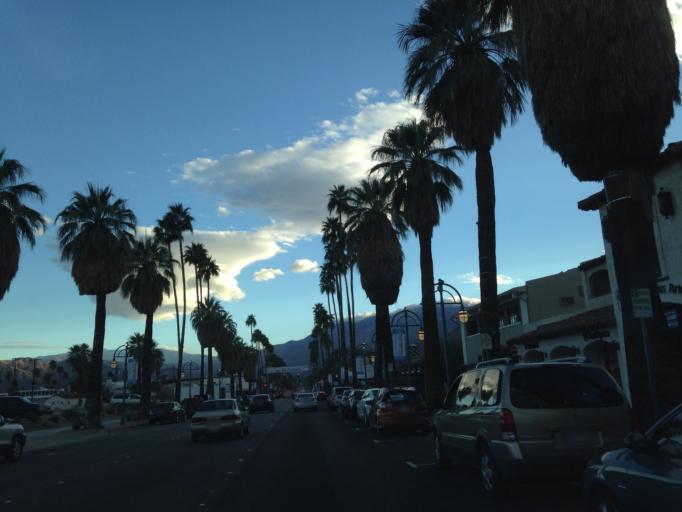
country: US
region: California
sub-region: Riverside County
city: Palm Springs
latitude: 33.8299
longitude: -116.5469
